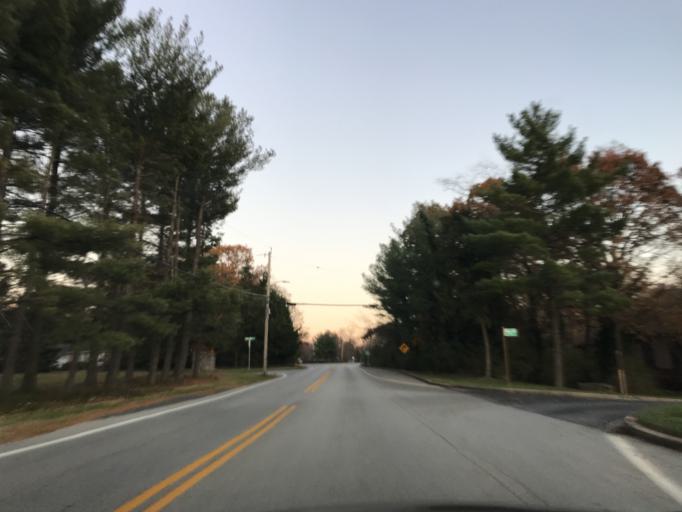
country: US
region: Maryland
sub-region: Howard County
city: West Elkridge
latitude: 39.2111
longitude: -76.7339
